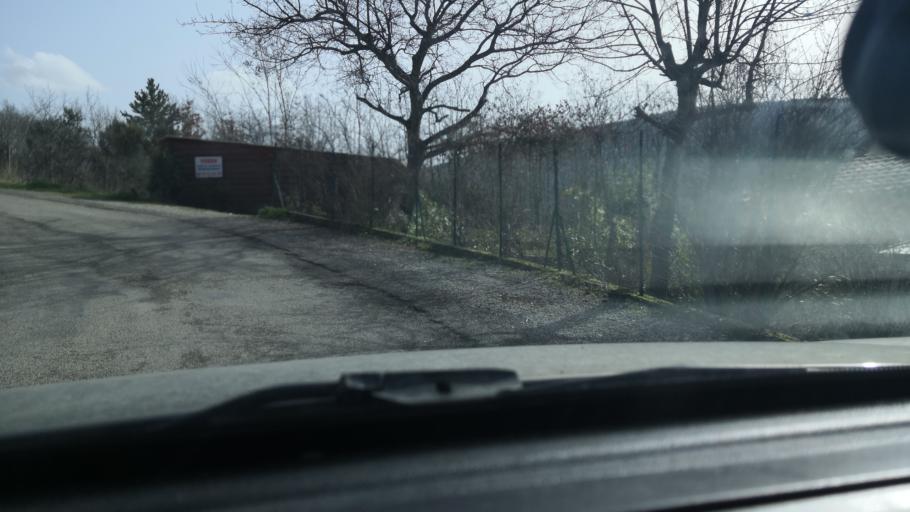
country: FR
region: Rhone-Alpes
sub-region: Departement de la Drome
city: Dieulefit
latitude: 44.5207
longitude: 5.0731
